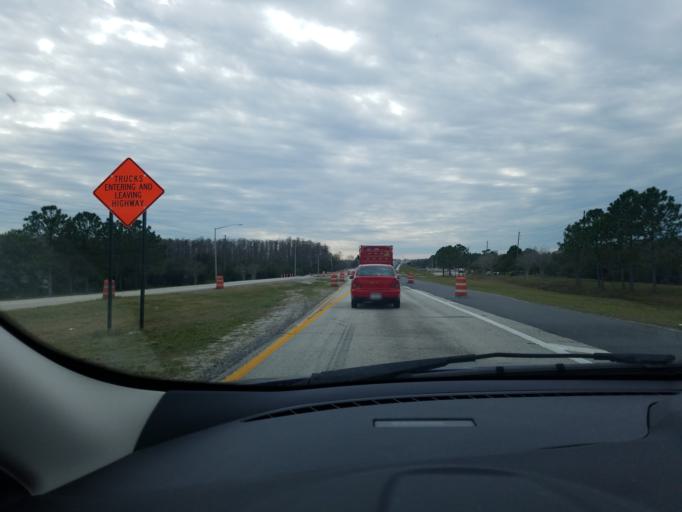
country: US
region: Florida
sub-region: Orange County
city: Meadow Woods
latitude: 28.3631
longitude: -81.3852
